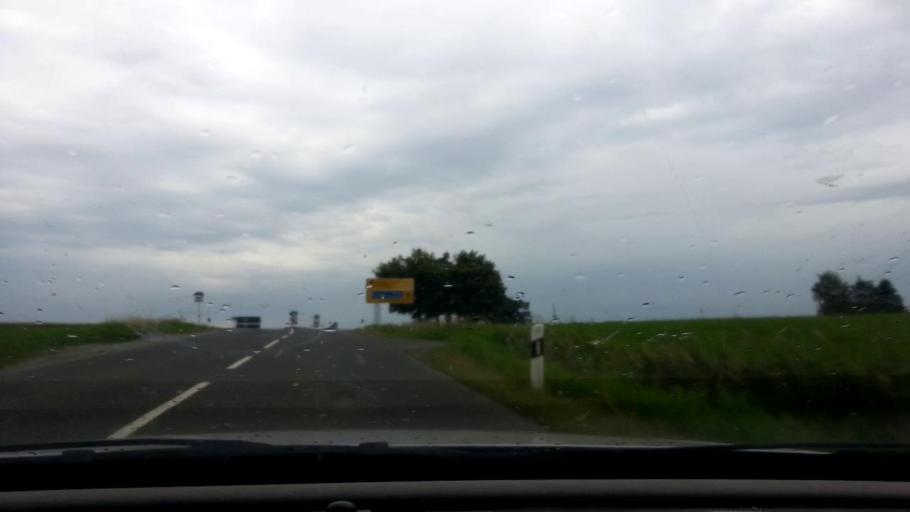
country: DE
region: Bavaria
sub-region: Upper Franconia
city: Speichersdorf
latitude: 49.8775
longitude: 11.8165
